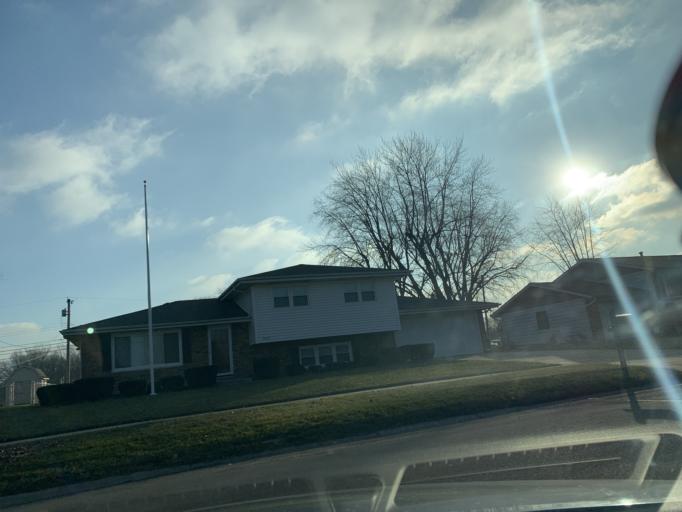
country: US
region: Indiana
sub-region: Porter County
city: Portage
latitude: 41.5745
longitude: -87.1685
